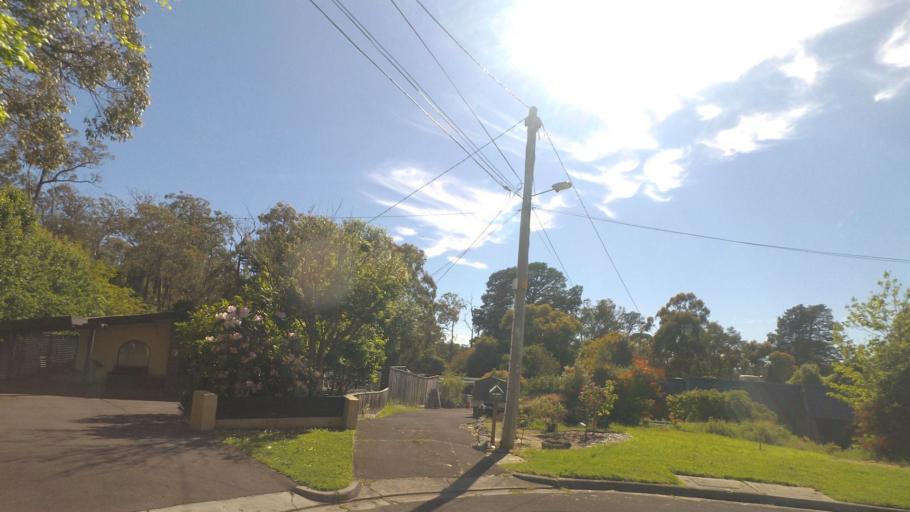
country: AU
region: Victoria
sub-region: Maroondah
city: Ringwood East
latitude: -37.8170
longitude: 145.2591
